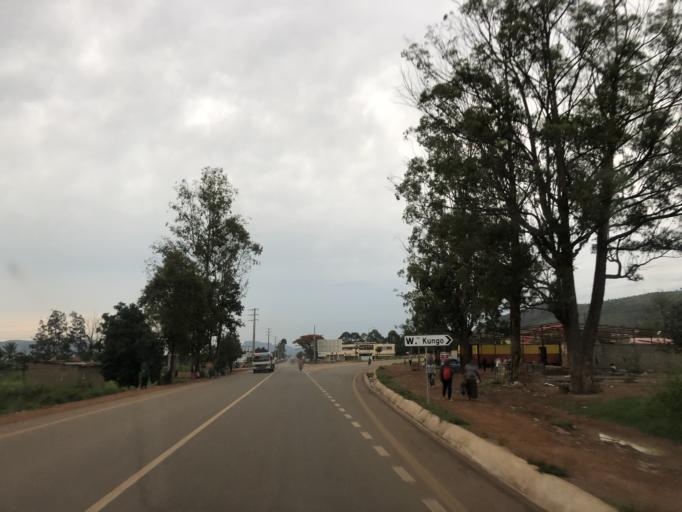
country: AO
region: Cuanza Sul
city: Uacu Cungo
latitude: -11.3541
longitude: 15.1210
